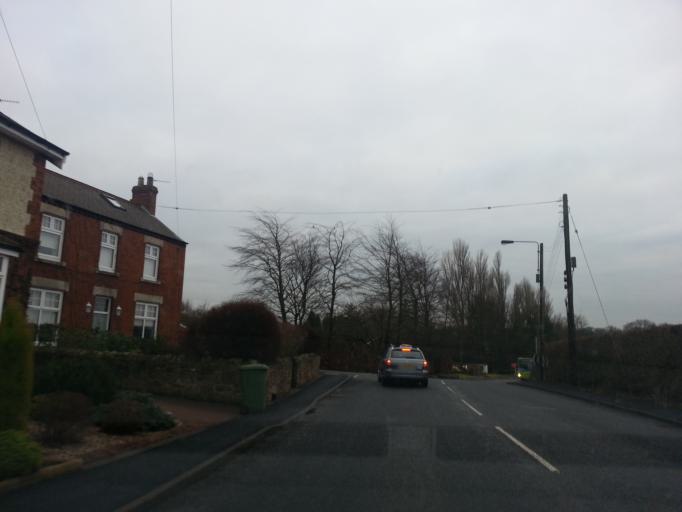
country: GB
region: England
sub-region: County Durham
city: Chester-le-Street
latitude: 54.8760
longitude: -1.5620
